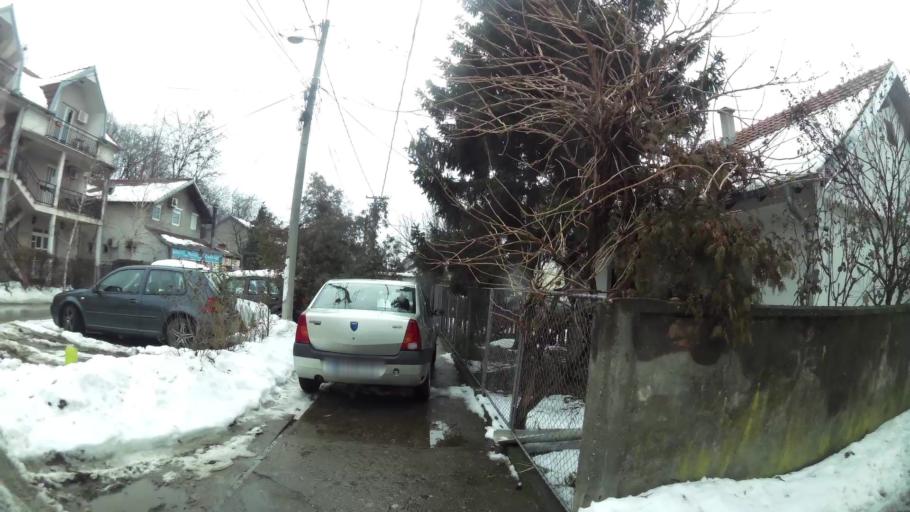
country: RS
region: Central Serbia
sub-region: Belgrade
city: Zemun
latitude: 44.8322
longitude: 20.3808
